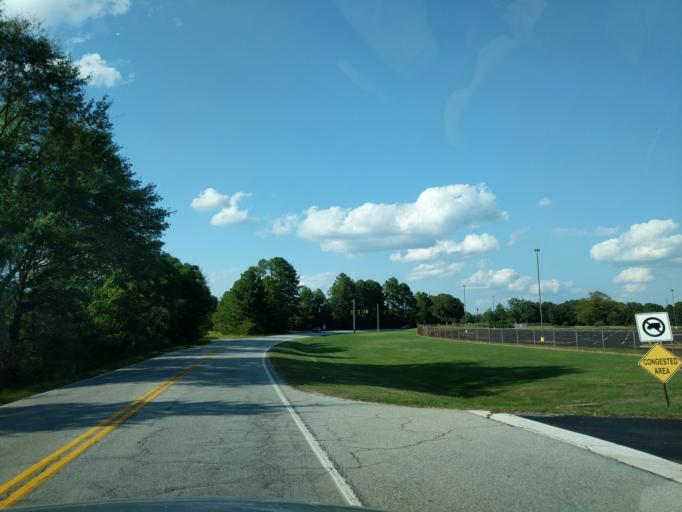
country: US
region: South Carolina
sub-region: Greenville County
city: Fountain Inn
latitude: 34.6841
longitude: -82.2203
